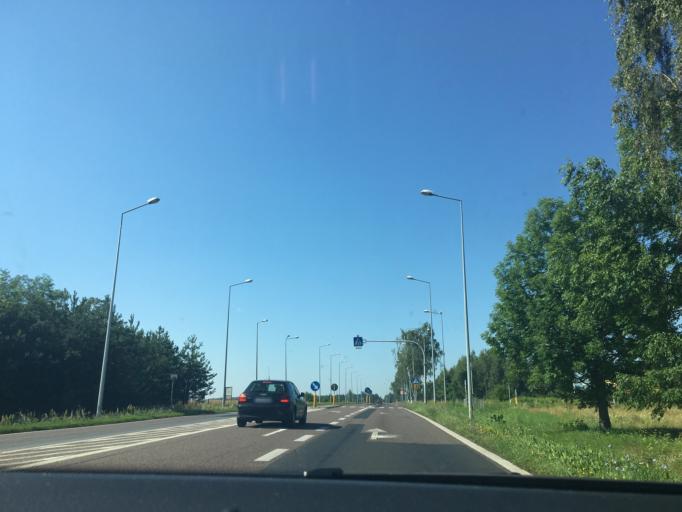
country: PL
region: Lublin Voivodeship
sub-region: Powiat radzynski
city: Borki
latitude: 51.7181
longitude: 22.5281
